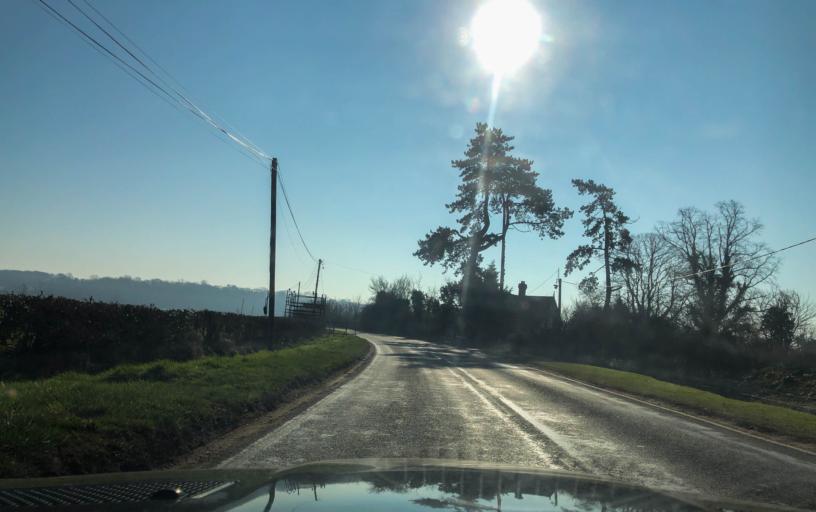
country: GB
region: England
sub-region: Warwickshire
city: Wellesbourne Mountford
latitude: 52.1884
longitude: -1.5826
